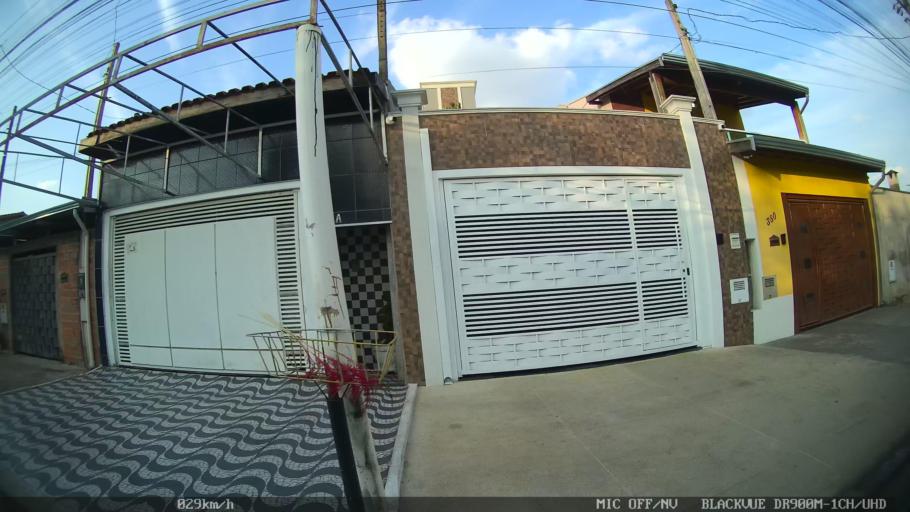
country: BR
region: Sao Paulo
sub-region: Hortolandia
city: Hortolandia
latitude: -22.8820
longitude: -47.1495
